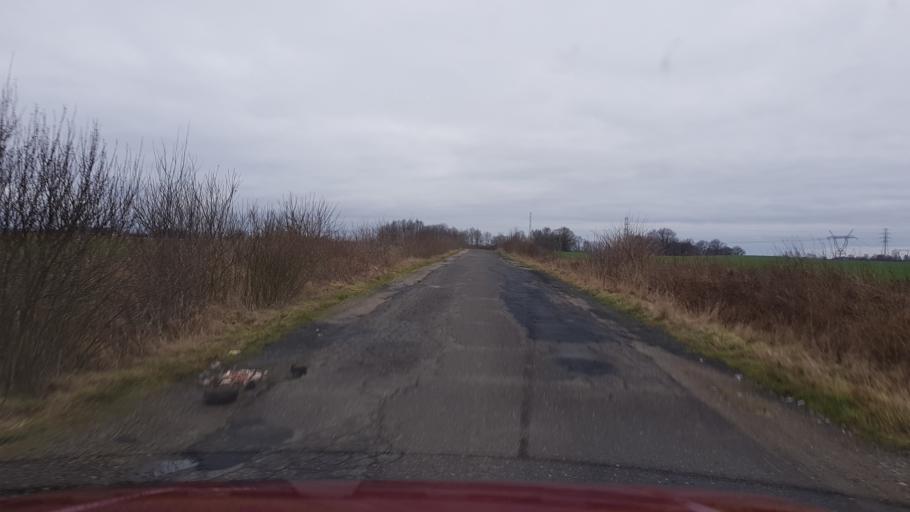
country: PL
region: West Pomeranian Voivodeship
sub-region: Powiat koszalinski
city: Mielno
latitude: 54.1523
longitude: 16.0317
